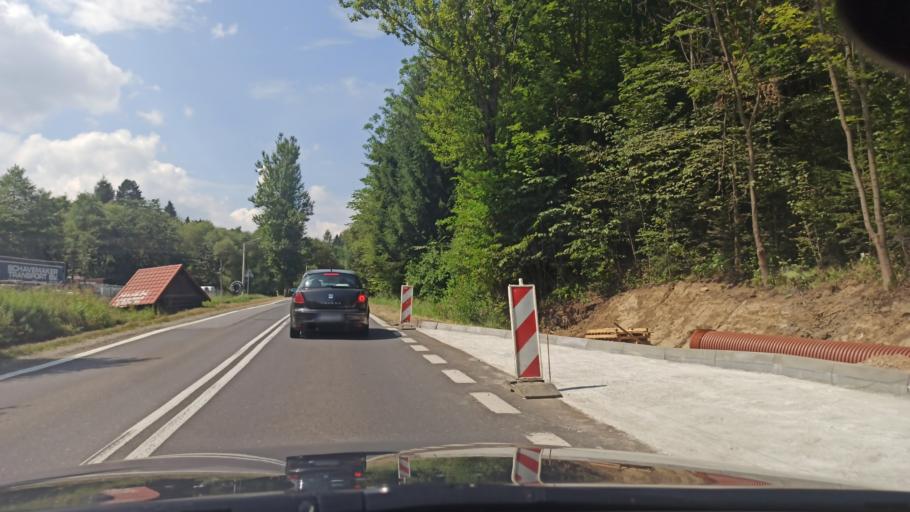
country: PL
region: Lesser Poland Voivodeship
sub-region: Powiat nowotarski
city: Krosnica
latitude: 49.4377
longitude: 20.3622
